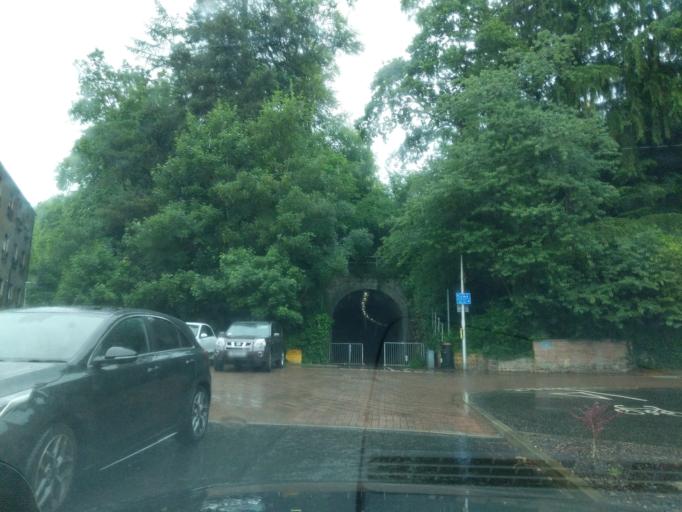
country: GB
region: Scotland
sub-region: Midlothian
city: Penicuik
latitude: 55.8425
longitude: -3.1948
